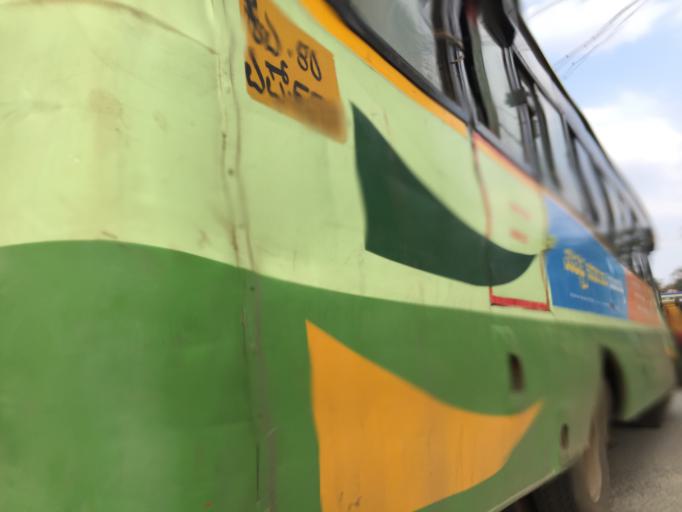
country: IN
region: Karnataka
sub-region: Chikkaballapur
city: Chik Ballapur
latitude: 13.4281
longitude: 77.7265
